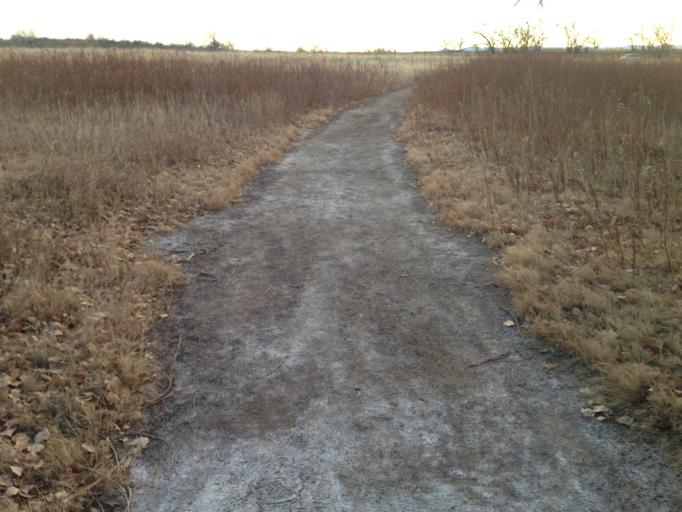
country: US
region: Colorado
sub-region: Adams County
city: Derby
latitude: 39.8138
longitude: -104.8528
